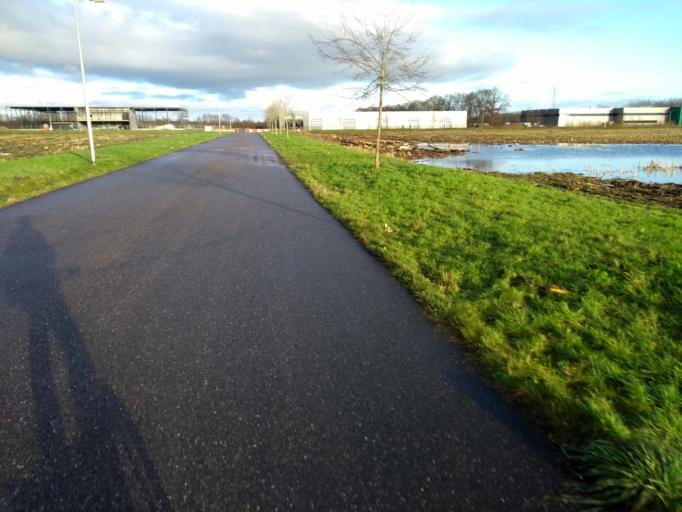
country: NL
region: Overijssel
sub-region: Gemeente Wierden
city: Wierden
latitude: 52.3850
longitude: 6.6036
